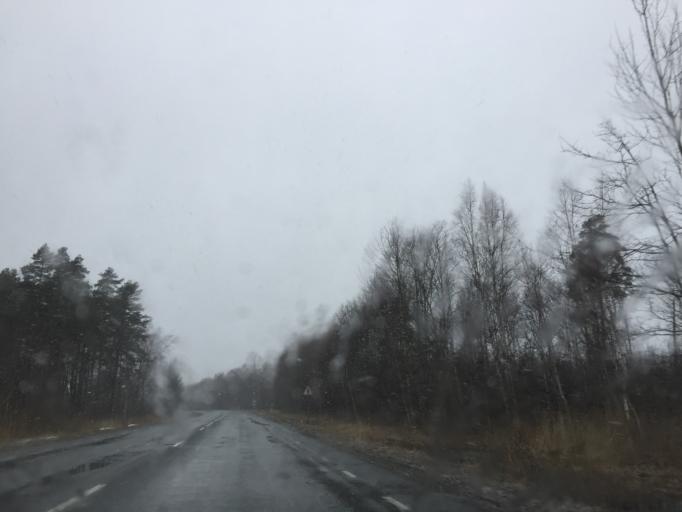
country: EE
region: Laeaene
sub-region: Ridala Parish
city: Uuemoisa
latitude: 58.8312
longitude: 23.6999
